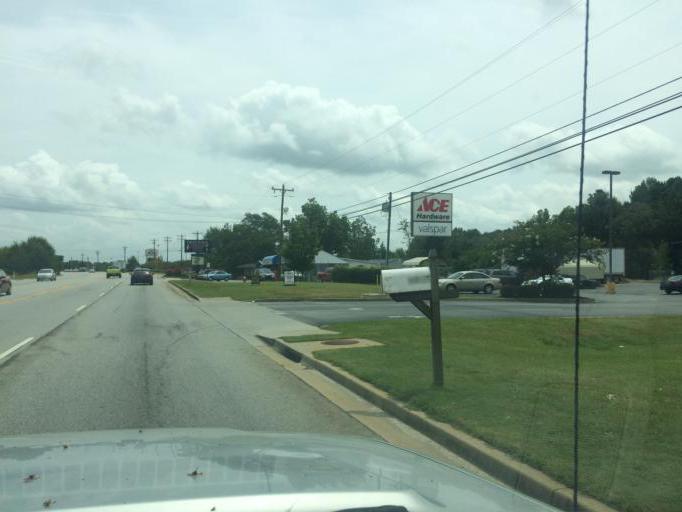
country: US
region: South Carolina
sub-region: Anderson County
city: Centerville
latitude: 34.5129
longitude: -82.7640
